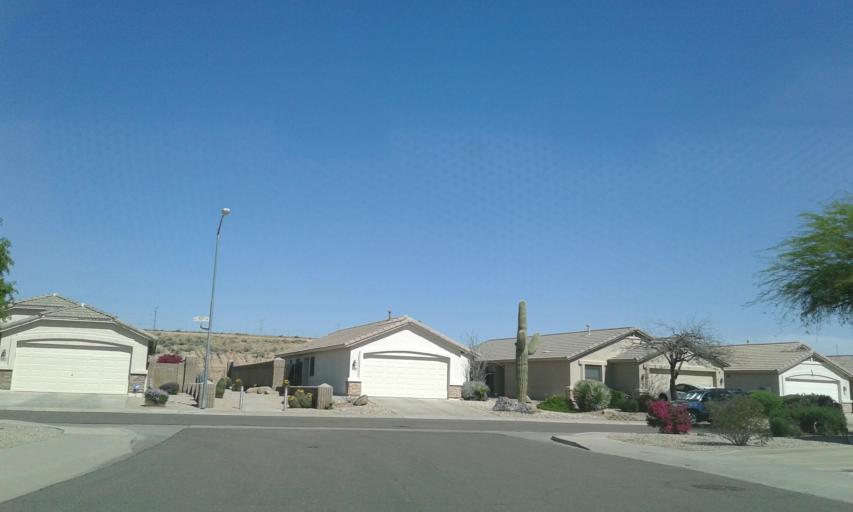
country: US
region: Arizona
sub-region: Maricopa County
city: Paradise Valley
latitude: 33.6677
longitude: -112.0078
